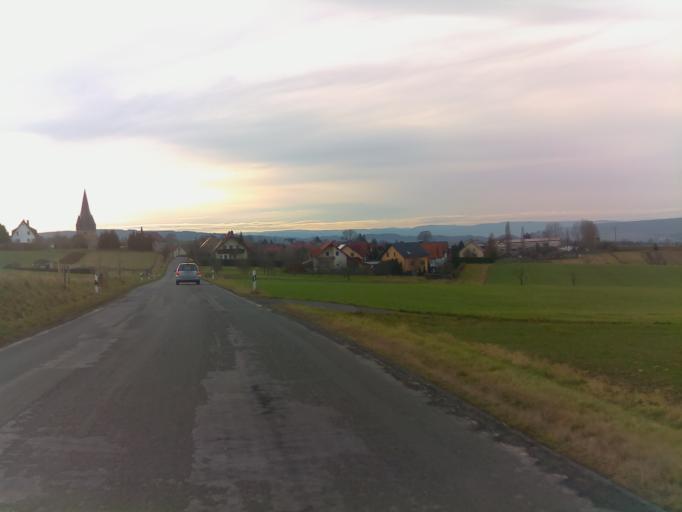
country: DE
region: Thuringia
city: Weira
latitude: 50.7065
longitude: 11.7237
